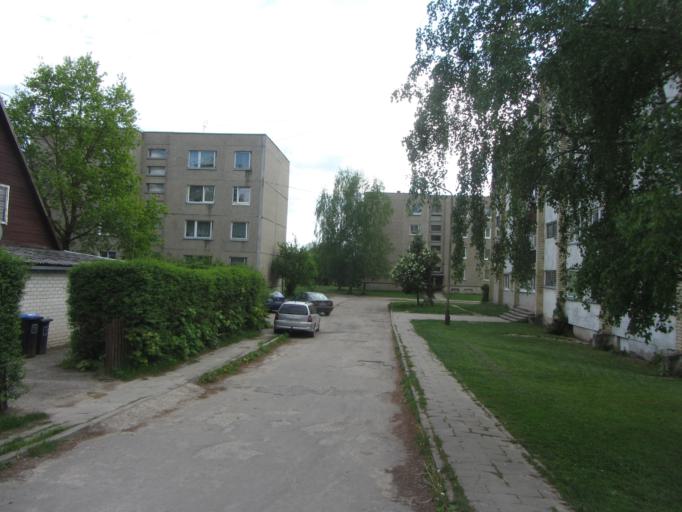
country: LT
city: Sirvintos
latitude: 55.0500
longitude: 24.9524
